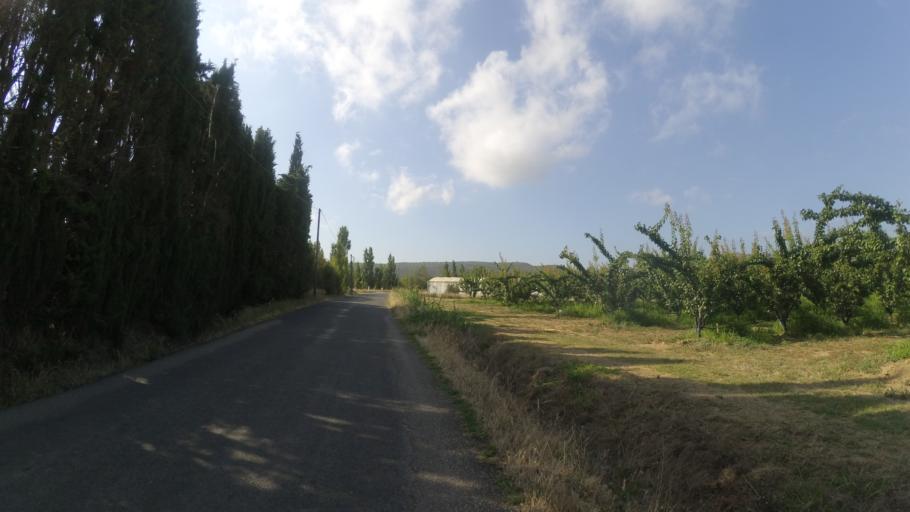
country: FR
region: Languedoc-Roussillon
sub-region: Departement des Pyrenees-Orientales
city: Millas
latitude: 42.6531
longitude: 2.7084
